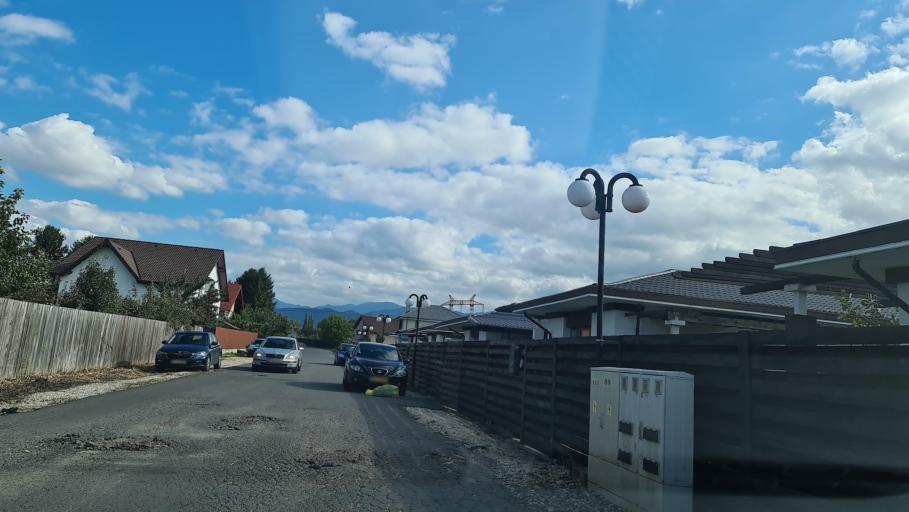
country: RO
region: Brasov
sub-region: Comuna Ghimbav
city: Ghimbav
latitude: 45.6975
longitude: 25.5489
